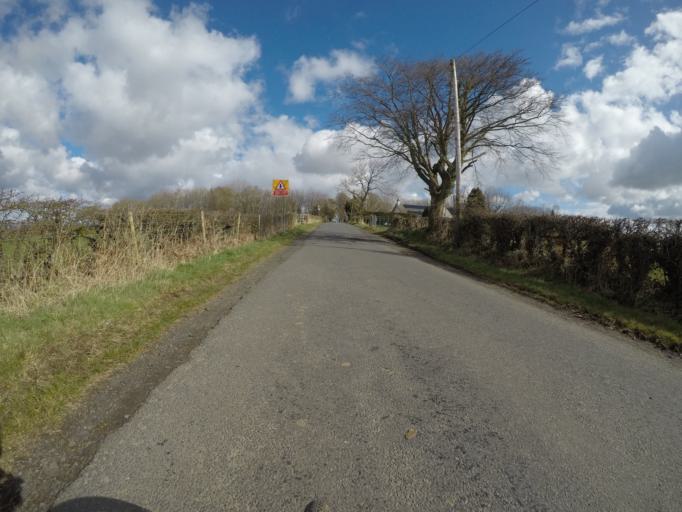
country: GB
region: Scotland
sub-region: North Ayrshire
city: Beith
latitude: 55.7183
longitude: -4.6197
